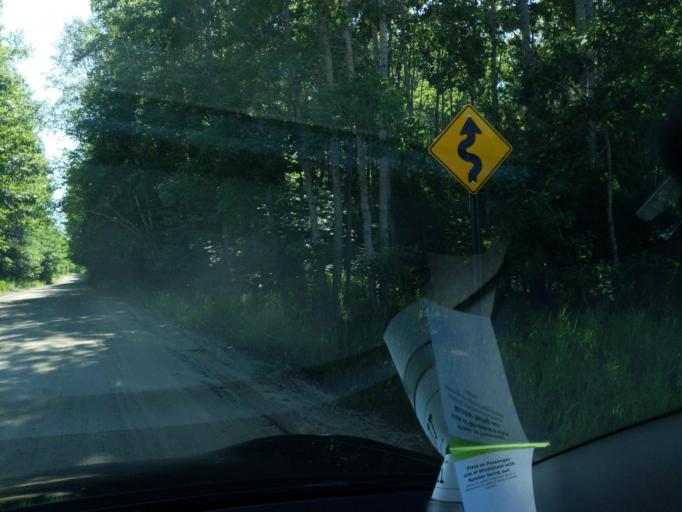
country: US
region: Michigan
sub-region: Mackinac County
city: Saint Ignace
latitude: 45.6795
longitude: -84.6887
